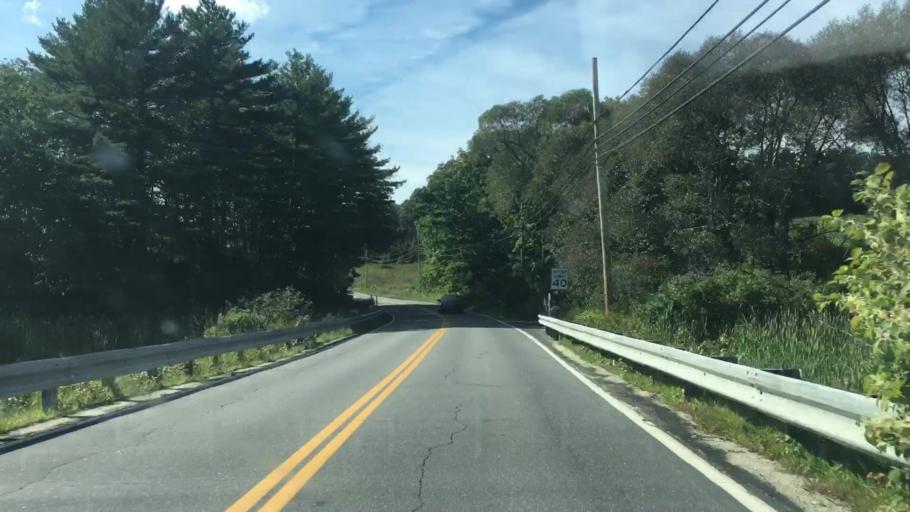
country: US
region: Maine
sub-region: Sagadahoc County
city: North Bath
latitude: 43.9325
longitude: -69.8649
